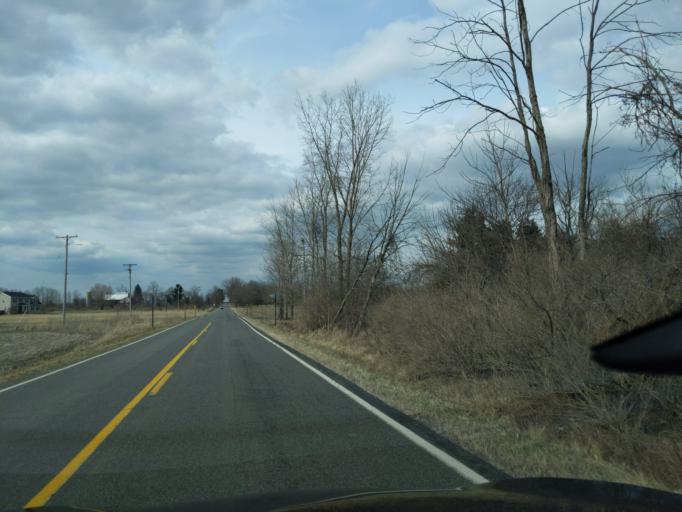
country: US
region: Michigan
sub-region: Ingham County
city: Mason
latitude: 42.5449
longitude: -84.4831
